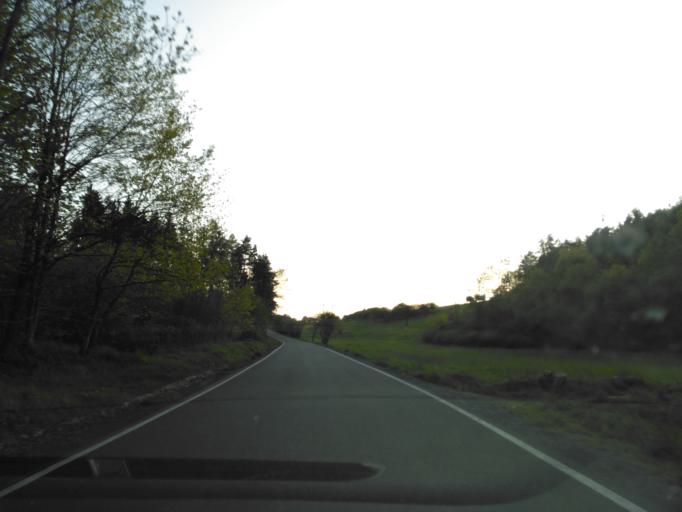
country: CZ
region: Central Bohemia
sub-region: Okres Beroun
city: Kraluv Dvur
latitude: 49.9179
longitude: 14.0388
